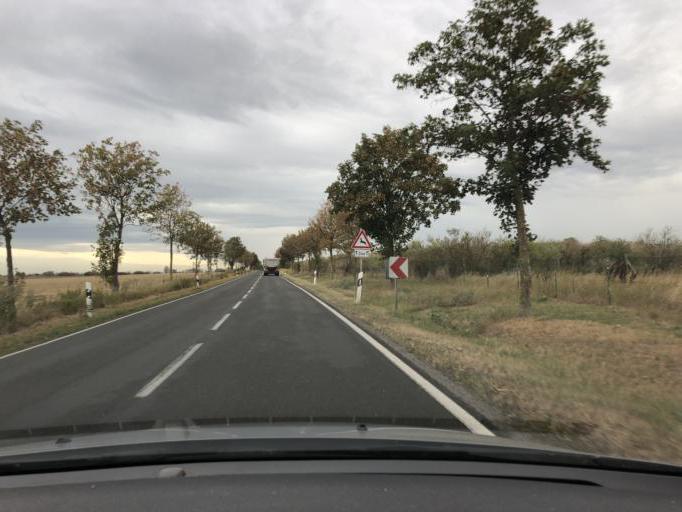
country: DE
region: Saxony-Anhalt
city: Nienburg/Saale
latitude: 51.8430
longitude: 11.7436
